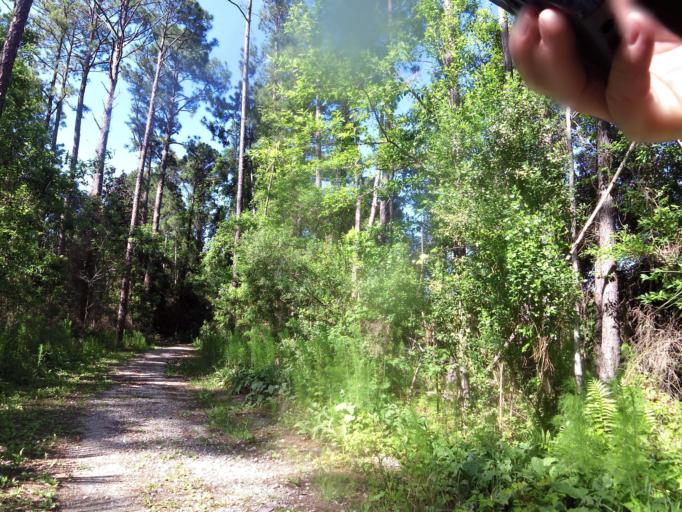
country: US
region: Florida
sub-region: Duval County
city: Atlantic Beach
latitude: 30.4598
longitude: -81.4865
